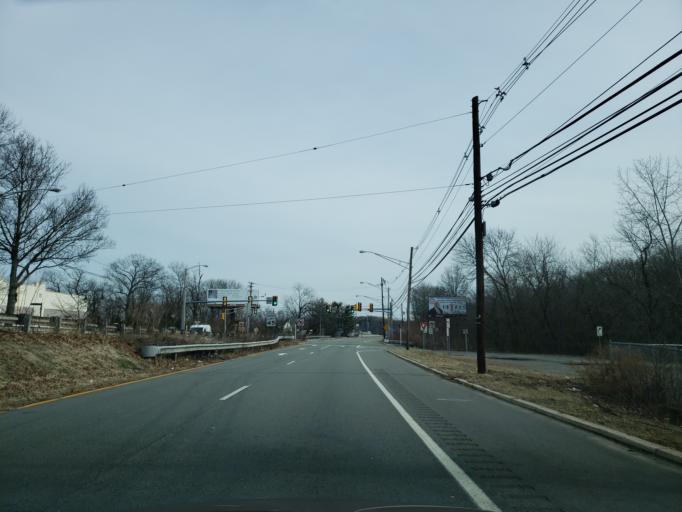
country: US
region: New Jersey
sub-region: Essex County
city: Westville
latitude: 40.8592
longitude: -74.3227
